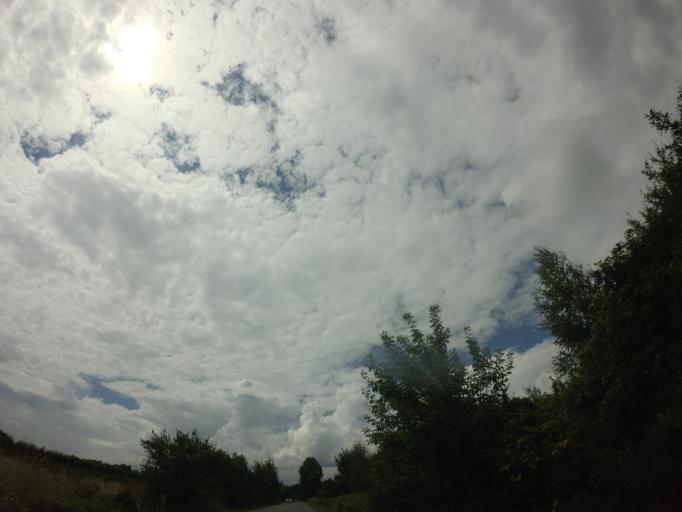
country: PL
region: Lublin Voivodeship
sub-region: Powiat pulawski
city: Kazimierz Dolny
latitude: 51.2742
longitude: 21.9303
